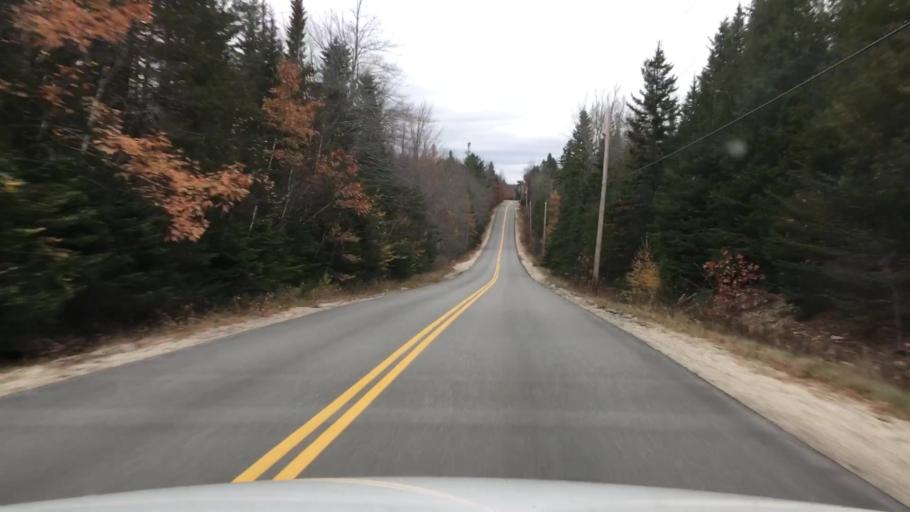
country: US
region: Maine
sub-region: Hancock County
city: Penobscot
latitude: 44.4492
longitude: -68.6369
